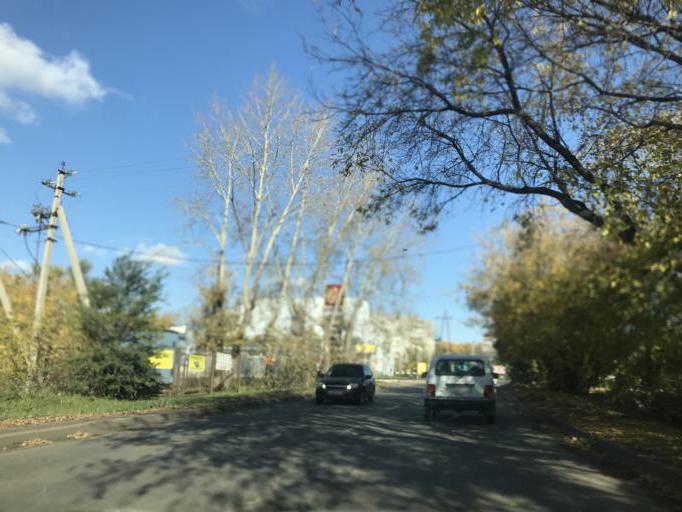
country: RU
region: Chelyabinsk
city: Dolgoderevenskoye
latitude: 55.2570
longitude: 61.3613
